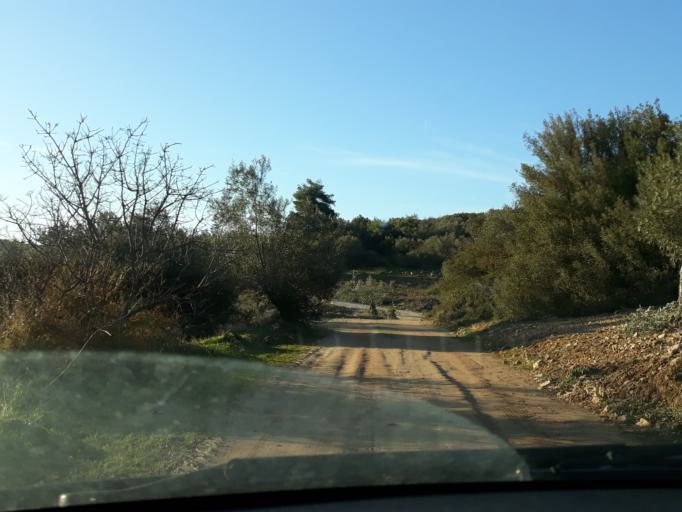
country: GR
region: Central Greece
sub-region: Nomos Voiotias
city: Asopia
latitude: 38.2643
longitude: 23.5350
